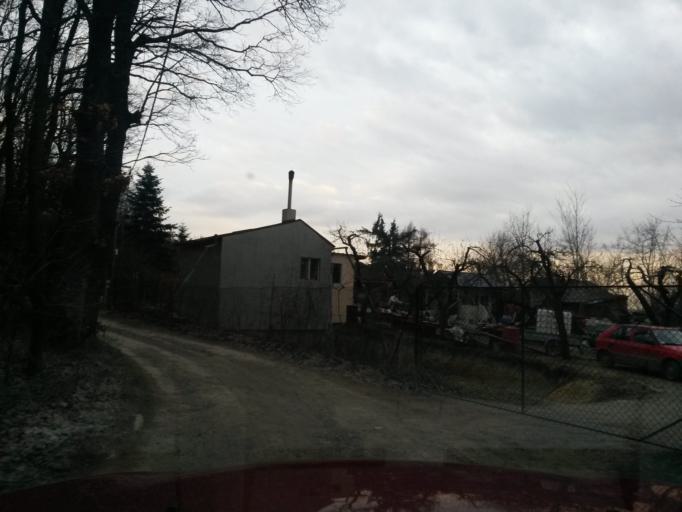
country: SK
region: Kosicky
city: Kosice
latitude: 48.7036
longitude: 21.2944
